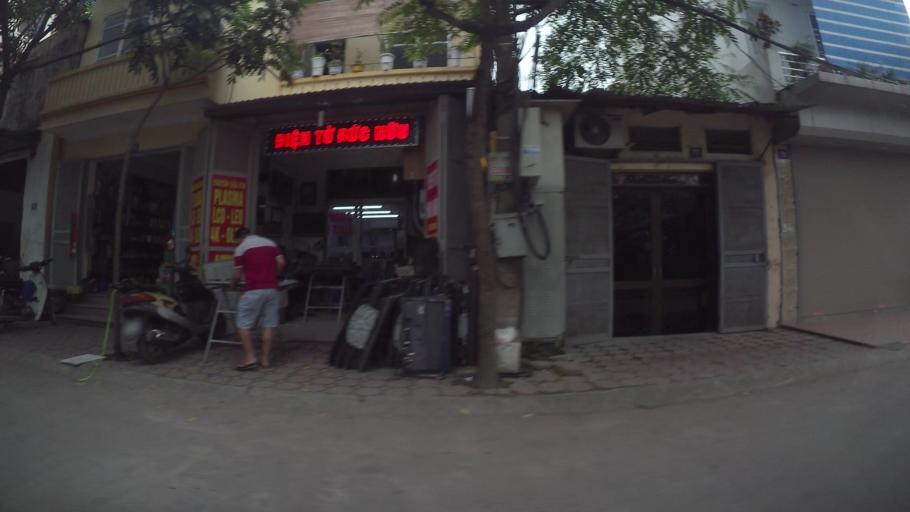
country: VN
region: Ha Noi
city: Hai BaTrung
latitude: 20.9961
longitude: 105.8830
